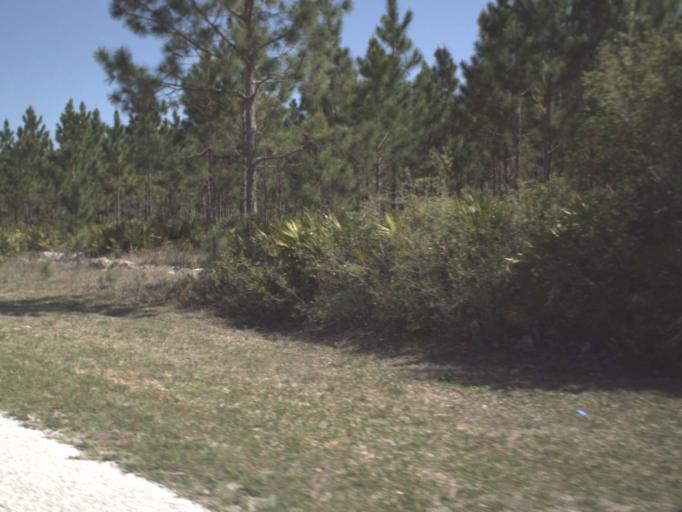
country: US
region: Florida
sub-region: Flagler County
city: Palm Coast
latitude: 29.6239
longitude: -81.2824
